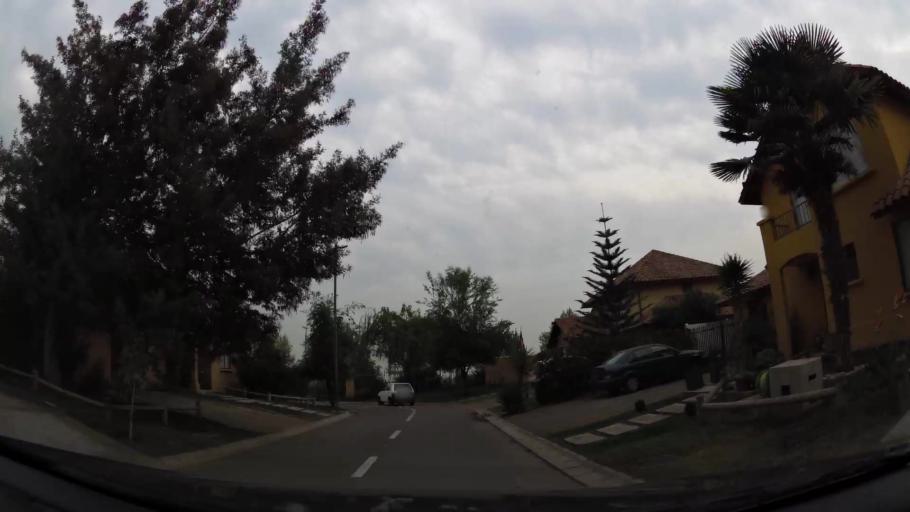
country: CL
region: Santiago Metropolitan
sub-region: Provincia de Chacabuco
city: Chicureo Abajo
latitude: -33.2015
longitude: -70.6526
